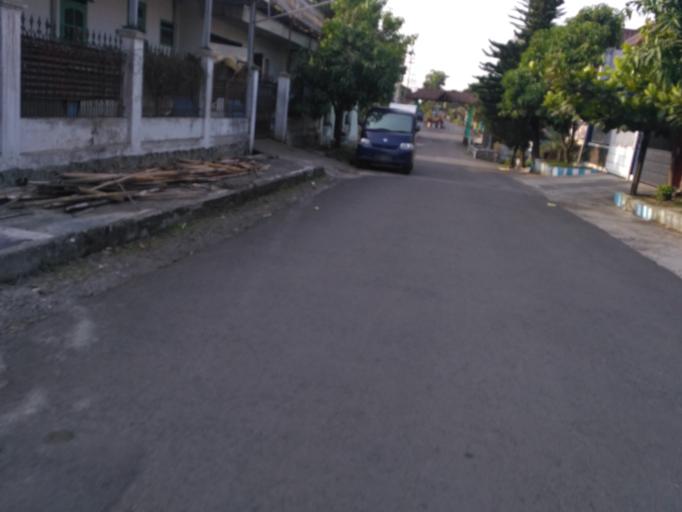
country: ID
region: East Java
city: Malang
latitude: -7.9371
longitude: 112.6311
